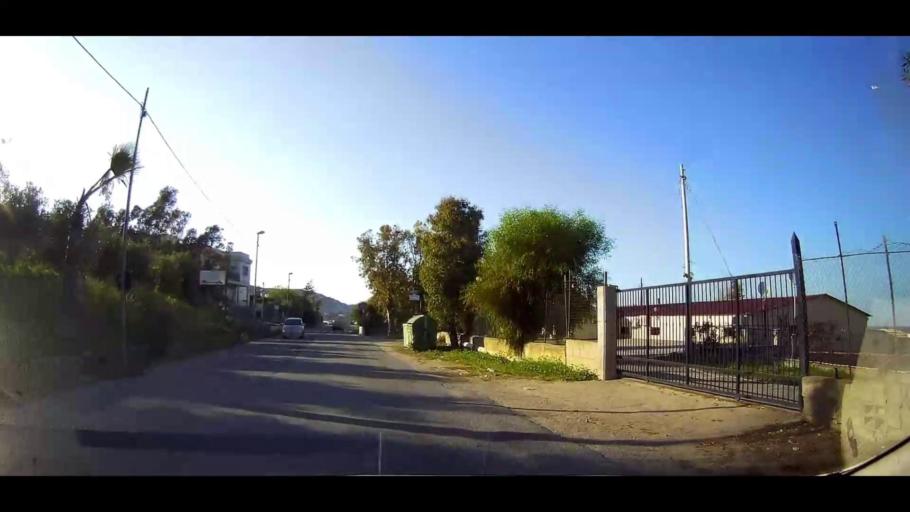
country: IT
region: Calabria
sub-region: Provincia di Crotone
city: Crotone
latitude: 39.0534
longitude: 17.1388
